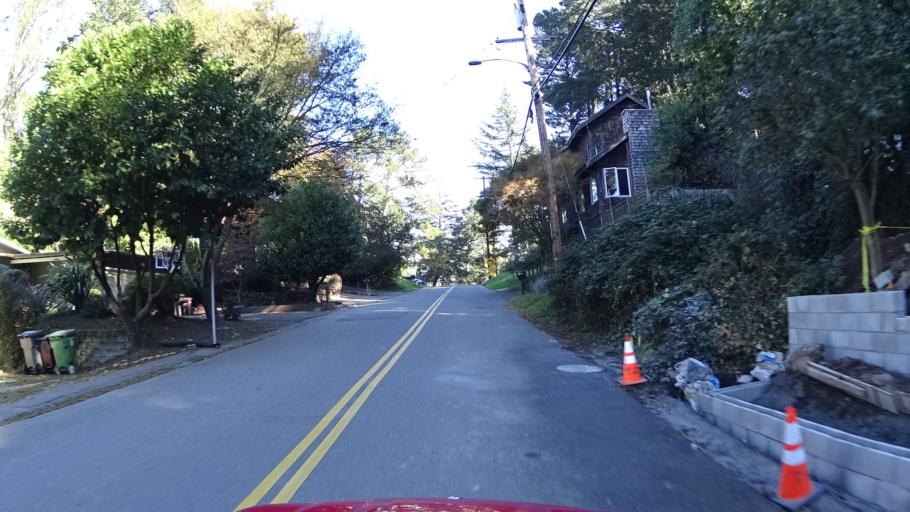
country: US
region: California
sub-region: Alameda County
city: Piedmont
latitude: 37.8339
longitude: -122.2025
